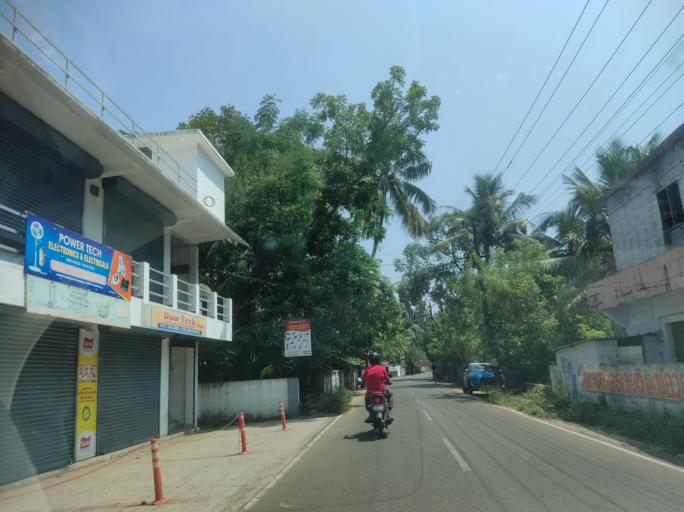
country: IN
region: Kerala
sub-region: Alappuzha
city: Kutiatodu
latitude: 9.7847
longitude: 76.3041
